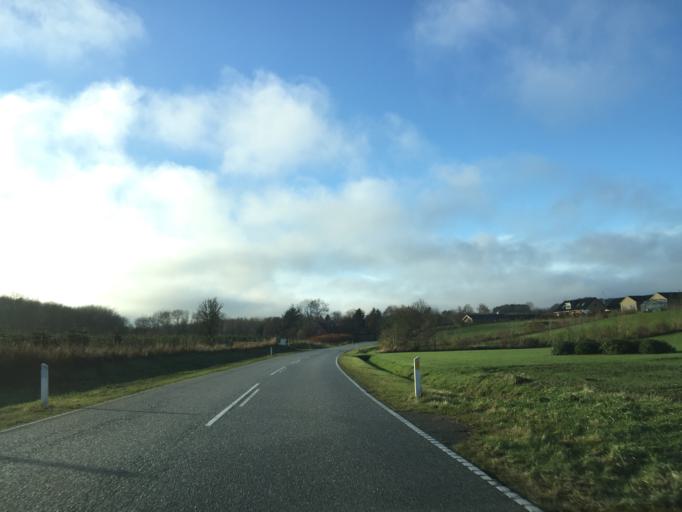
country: DK
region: Central Jutland
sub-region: Favrskov Kommune
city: Hammel
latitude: 56.1753
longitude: 9.8243
